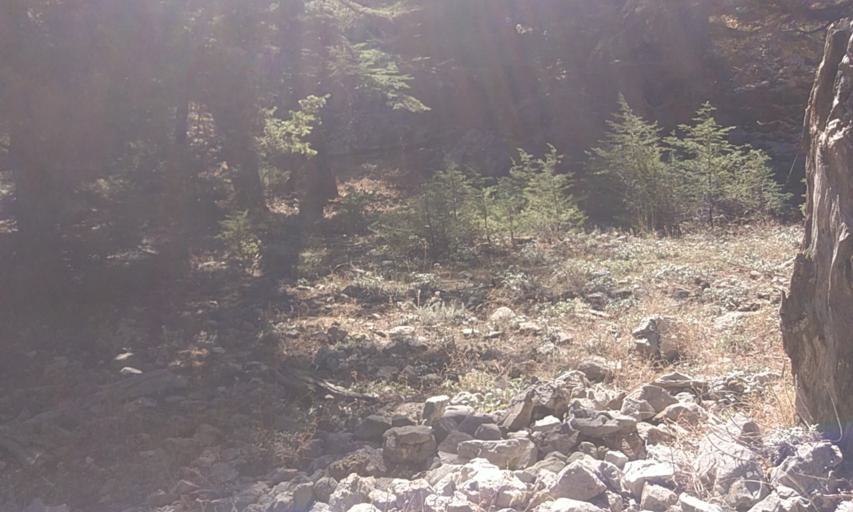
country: TR
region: Antalya
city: Altinyaka
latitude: 36.5569
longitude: 30.4150
